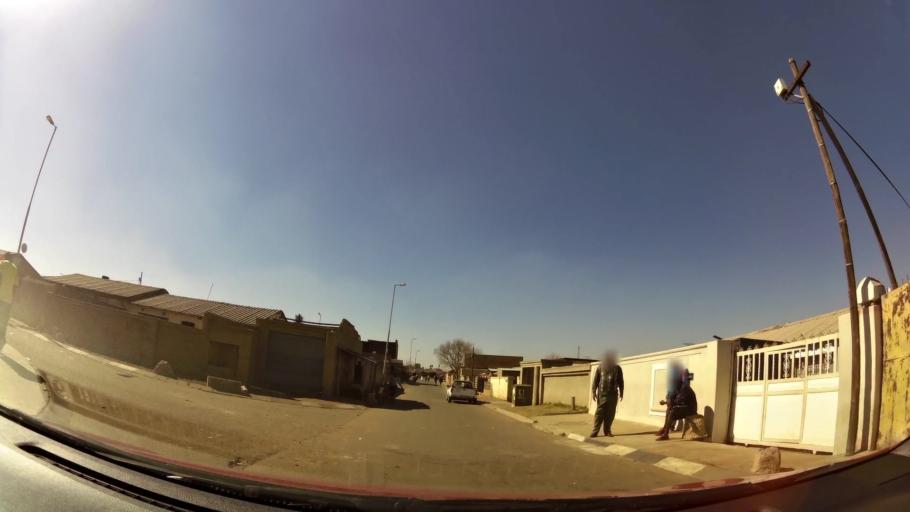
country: ZA
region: Gauteng
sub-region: City of Johannesburg Metropolitan Municipality
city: Soweto
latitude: -26.2400
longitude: 27.8454
